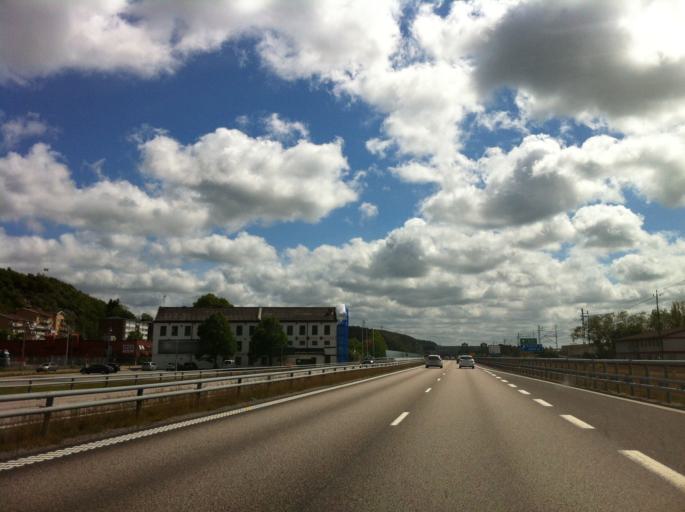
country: SE
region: Vaestra Goetaland
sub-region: Ale Kommun
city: Surte
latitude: 57.8670
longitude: 12.0233
